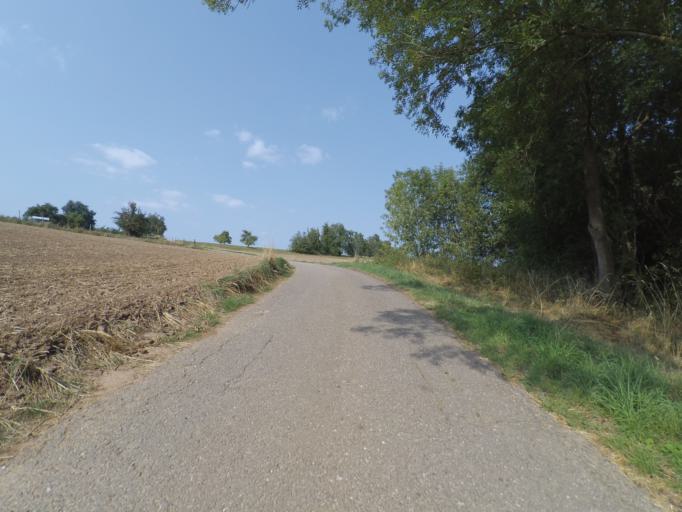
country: DE
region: Rheinland-Pfalz
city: Kirf
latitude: 49.5316
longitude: 6.5018
